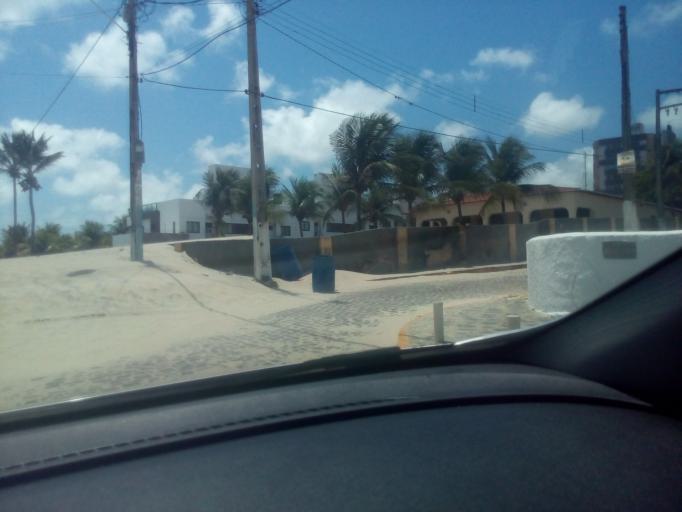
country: BR
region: Rio Grande do Norte
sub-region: Nisia Floresta
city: Nisia Floresta
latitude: -5.9715
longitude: -35.1267
